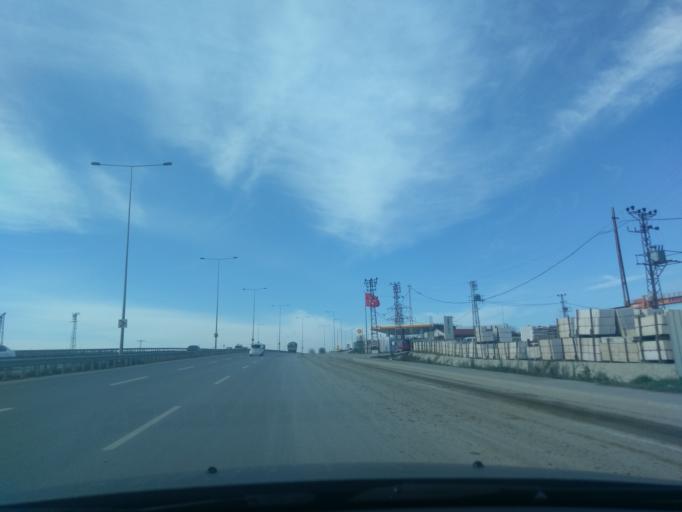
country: TR
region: Istanbul
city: Basaksehir
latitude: 41.1363
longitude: 28.8132
